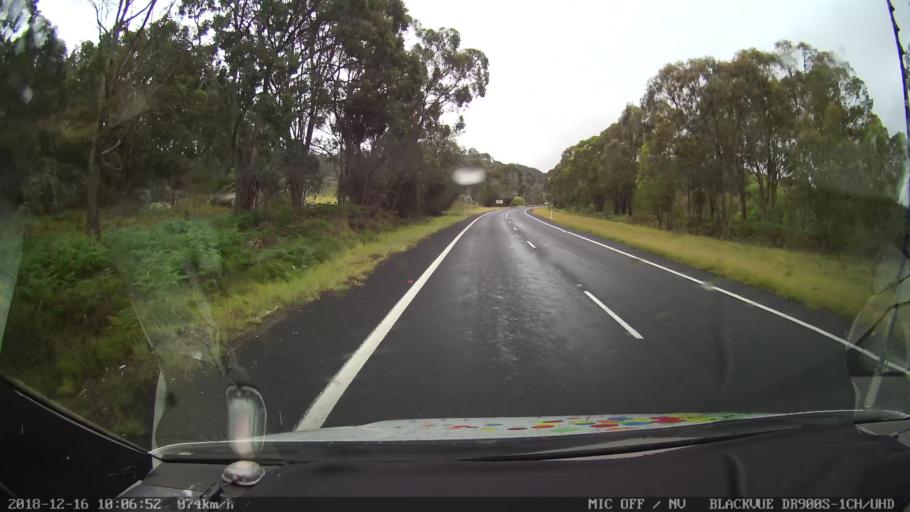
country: AU
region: New South Wales
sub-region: Glen Innes Severn
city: Glen Innes
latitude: -29.3406
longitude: 151.8926
